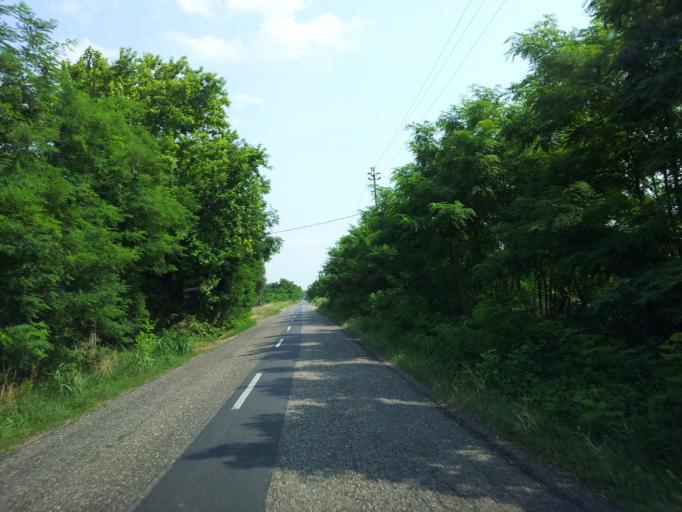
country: HU
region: Pest
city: Rackeve
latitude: 47.1939
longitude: 18.9263
